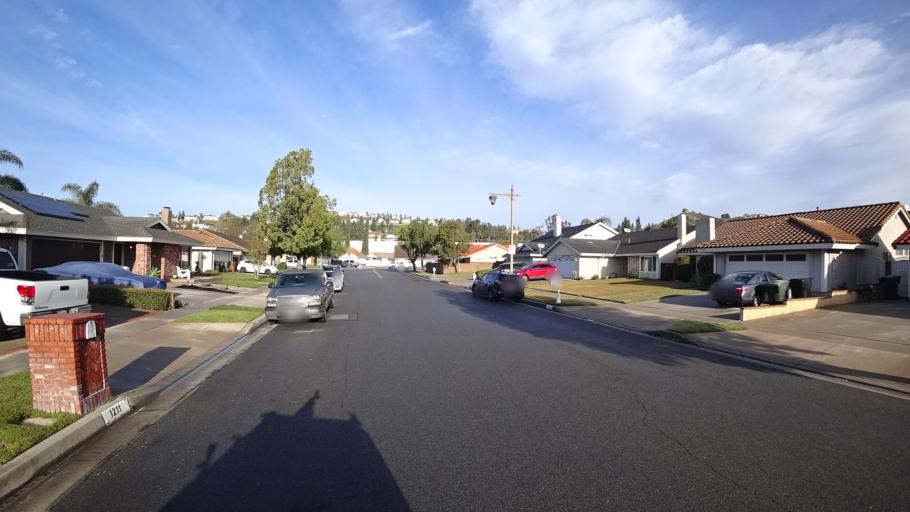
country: US
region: California
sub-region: Orange County
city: Yorba Linda
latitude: 33.8699
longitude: -117.7712
